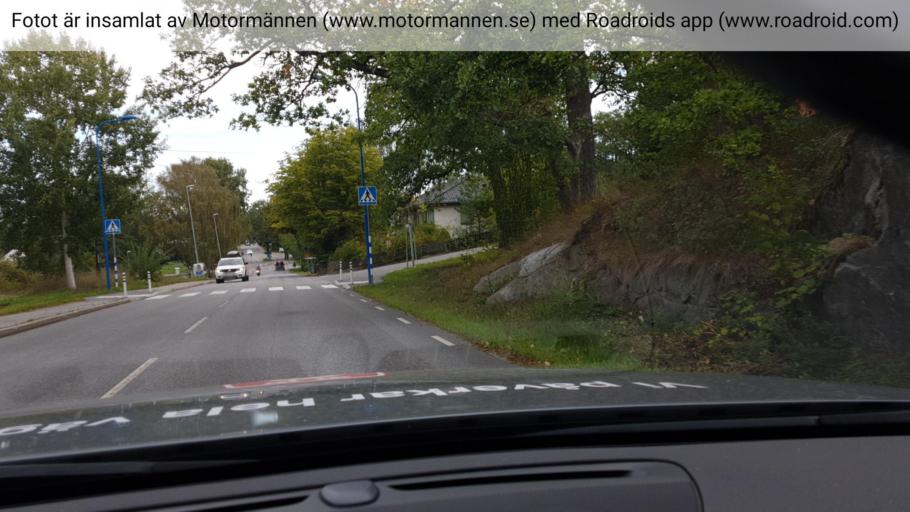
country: SE
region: Stockholm
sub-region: Danderyds Kommun
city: Djursholm
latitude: 59.3881
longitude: 18.0703
